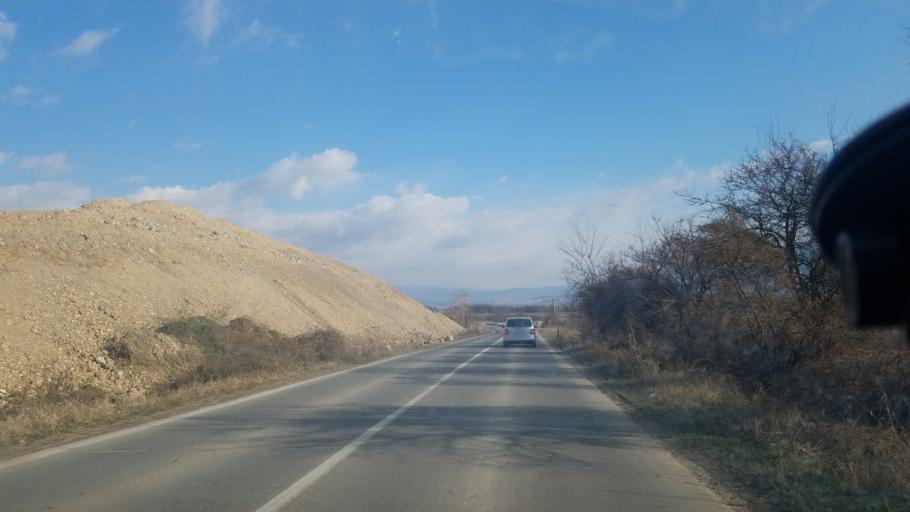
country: MK
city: Obleshevo
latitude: 41.8987
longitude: 22.3644
